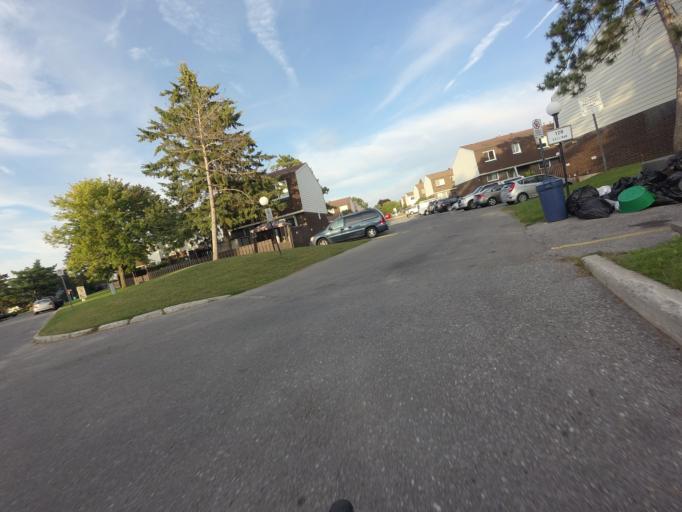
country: CA
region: Ontario
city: Ottawa
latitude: 45.3401
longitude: -75.7449
